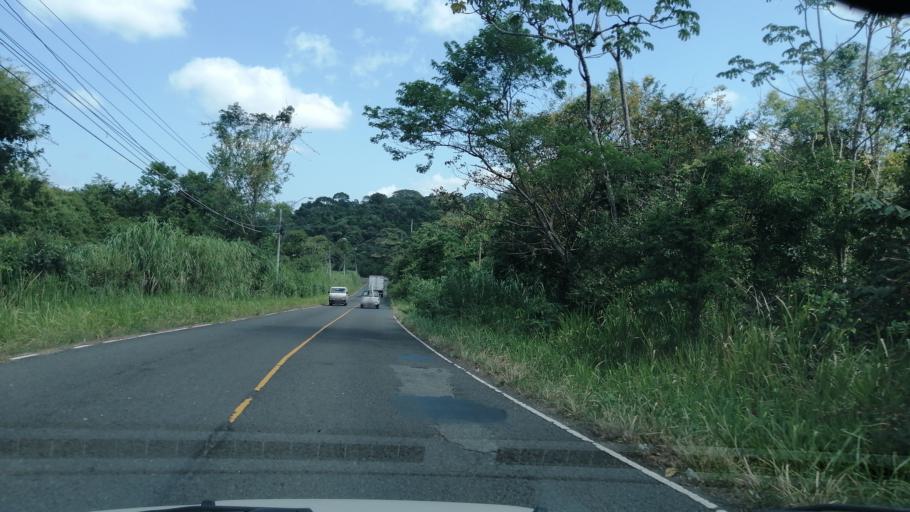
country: PA
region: Panama
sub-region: Distrito de Panama
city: Ancon
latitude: 8.9125
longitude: -79.5679
